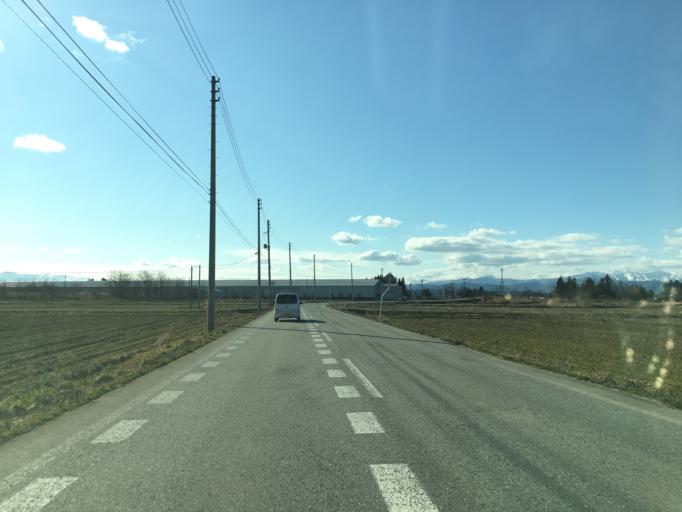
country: JP
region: Yamagata
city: Takahata
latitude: 38.0070
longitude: 140.0939
